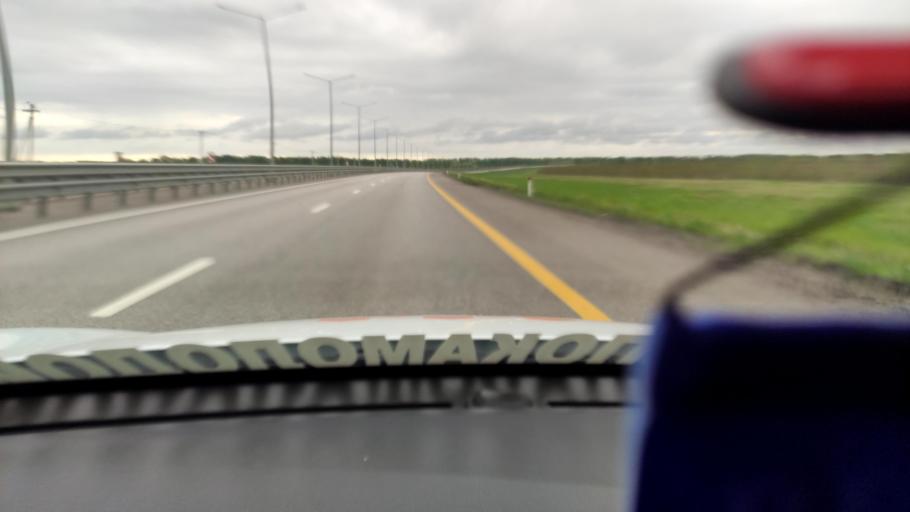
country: RU
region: Voronezj
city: Podkletnoye
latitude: 51.5866
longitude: 39.4475
